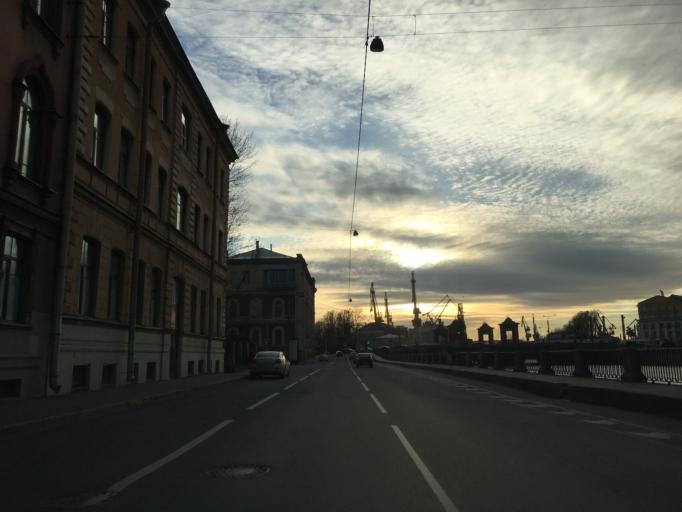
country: RU
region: St.-Petersburg
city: Admiralteisky
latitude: 59.9159
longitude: 30.2826
